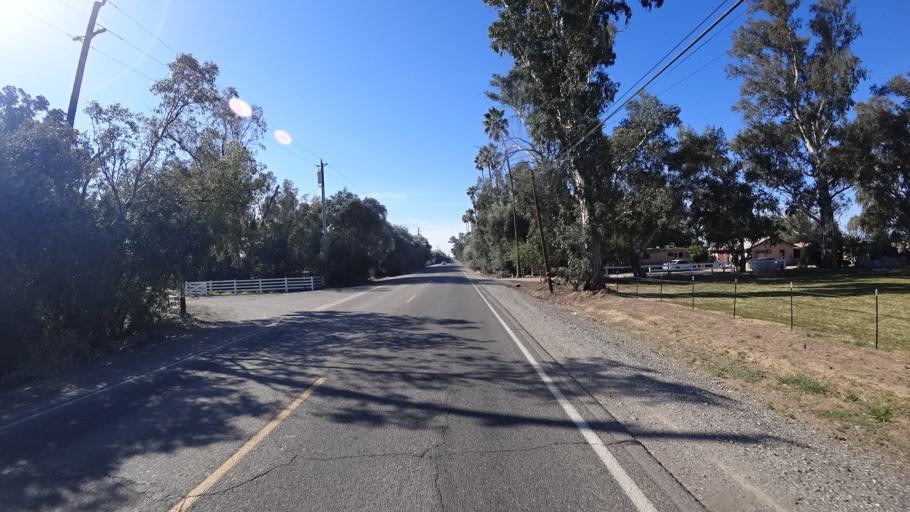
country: US
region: California
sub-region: Glenn County
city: Orland
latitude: 39.7082
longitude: -122.1970
